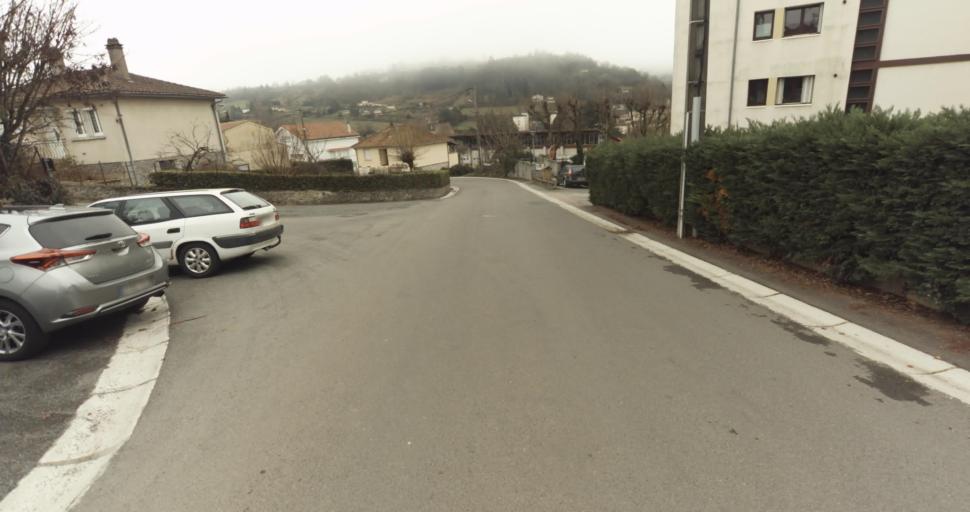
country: FR
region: Midi-Pyrenees
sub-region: Departement du Lot
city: Figeac
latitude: 44.6101
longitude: 2.0383
